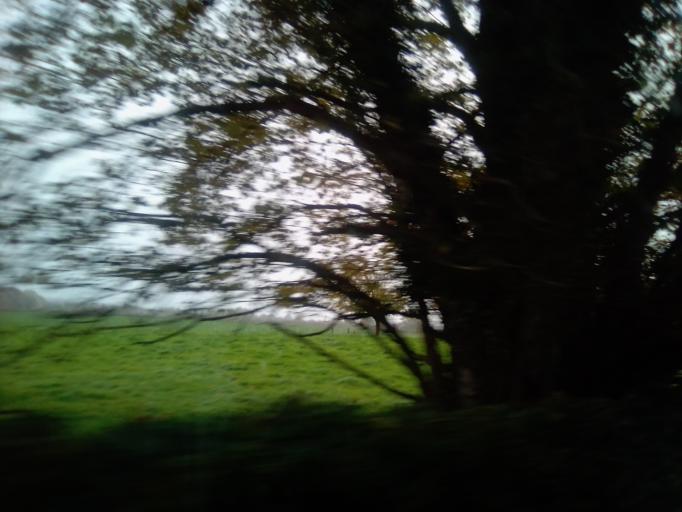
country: IE
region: Leinster
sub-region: Uibh Fhaili
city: Birr
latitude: 53.0230
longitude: -7.9121
